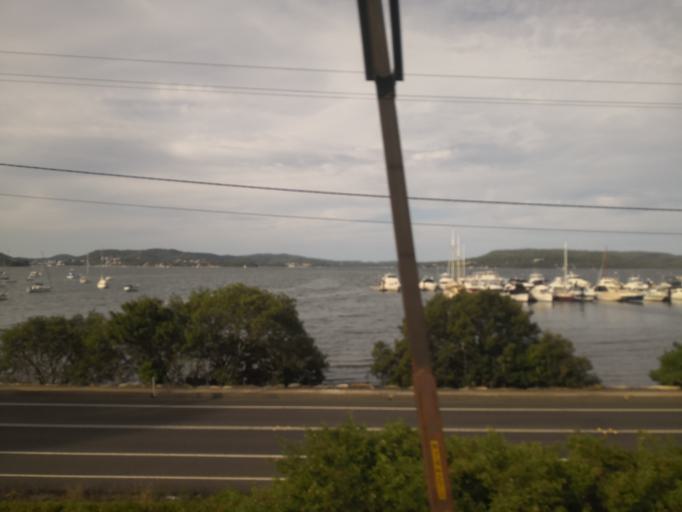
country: AU
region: New South Wales
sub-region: Gosford Shire
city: Point Clare
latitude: -33.4715
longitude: 151.3203
